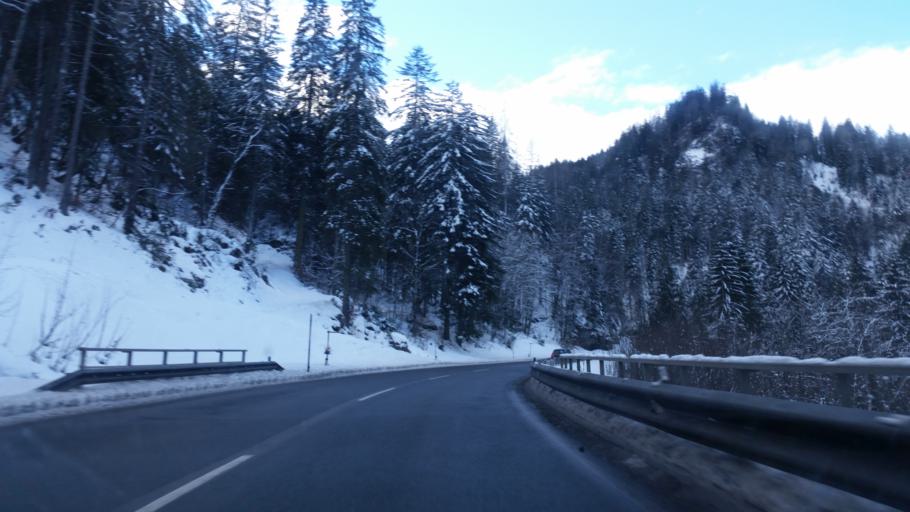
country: AT
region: Salzburg
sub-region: Politischer Bezirk Sankt Johann im Pongau
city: Untertauern
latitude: 47.2806
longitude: 13.5051
